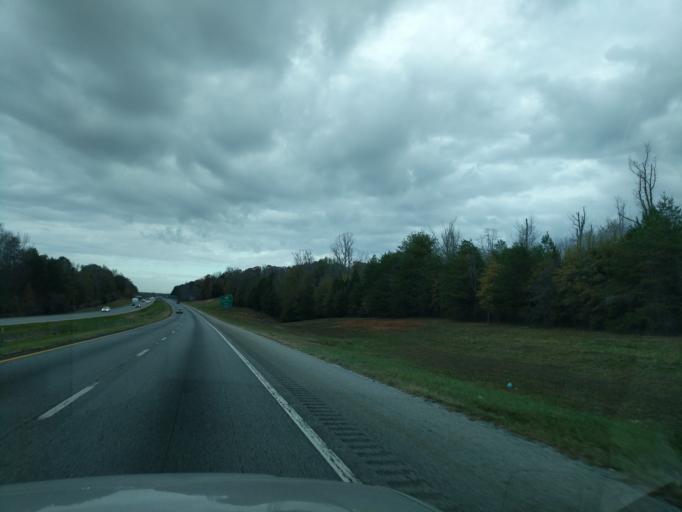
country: US
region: South Carolina
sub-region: Spartanburg County
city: Roebuck
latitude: 34.8212
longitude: -81.9637
